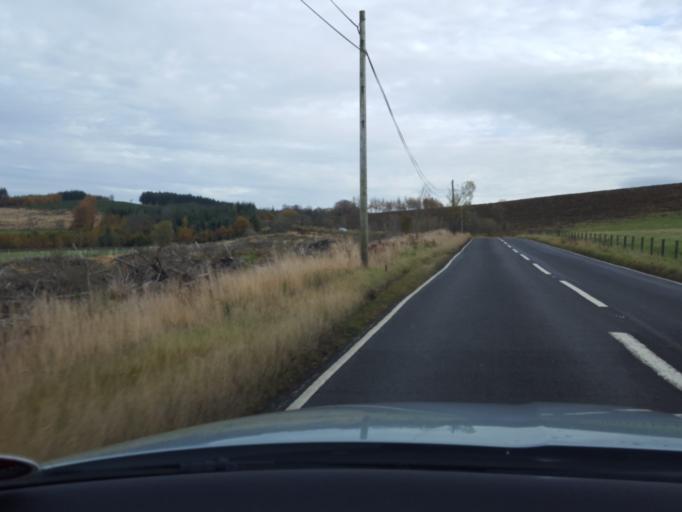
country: GB
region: Scotland
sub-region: South Lanarkshire
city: Biggar
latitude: 55.6843
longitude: -3.4394
